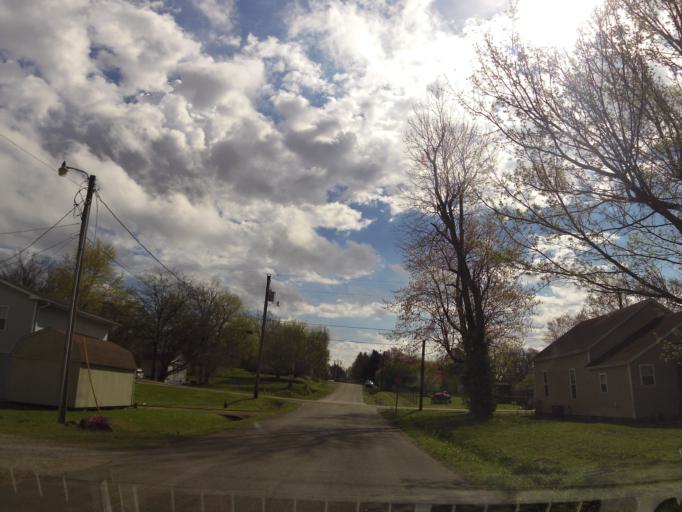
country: US
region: Missouri
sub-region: Butler County
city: Poplar Bluff
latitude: 36.7632
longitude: -90.3910
